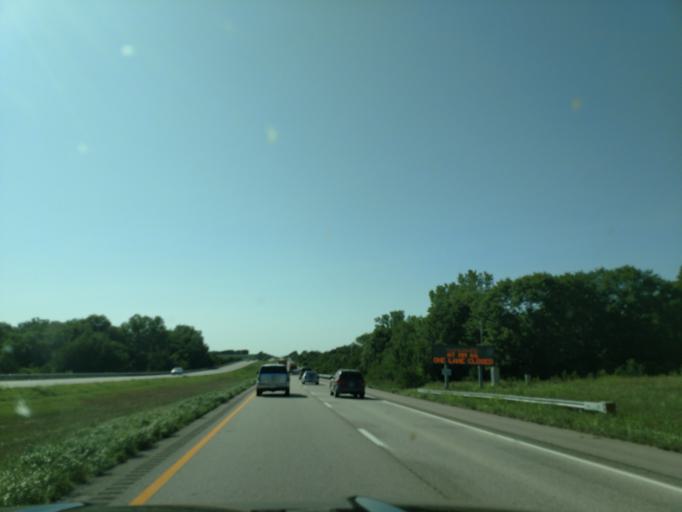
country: US
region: Missouri
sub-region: Andrew County
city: Country Club Village
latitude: 39.8680
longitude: -94.8266
